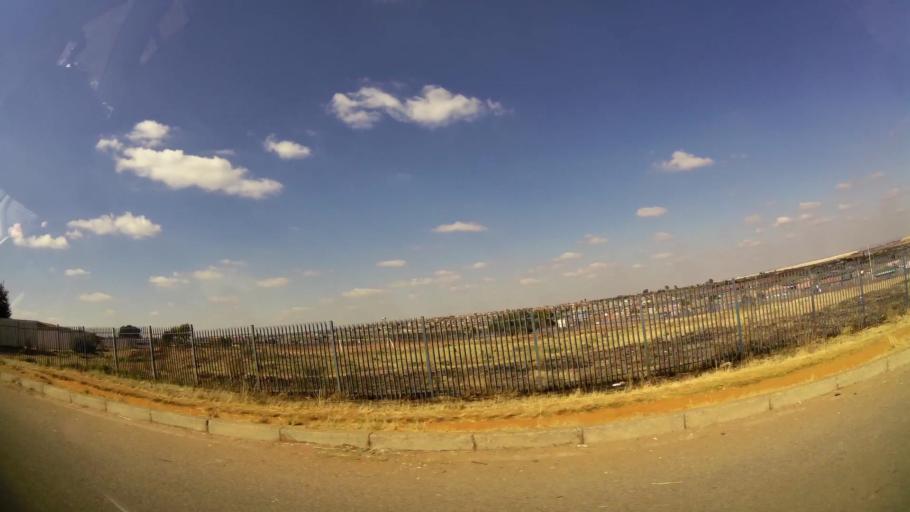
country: ZA
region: Gauteng
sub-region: West Rand District Municipality
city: Krugersdorp
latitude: -26.1674
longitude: 27.7827
